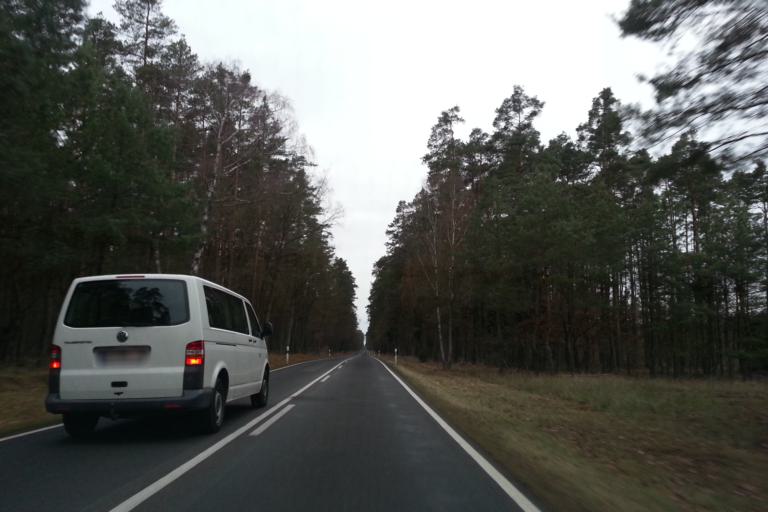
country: DE
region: Mecklenburg-Vorpommern
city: Jatznick
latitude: 53.6047
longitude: 13.9161
